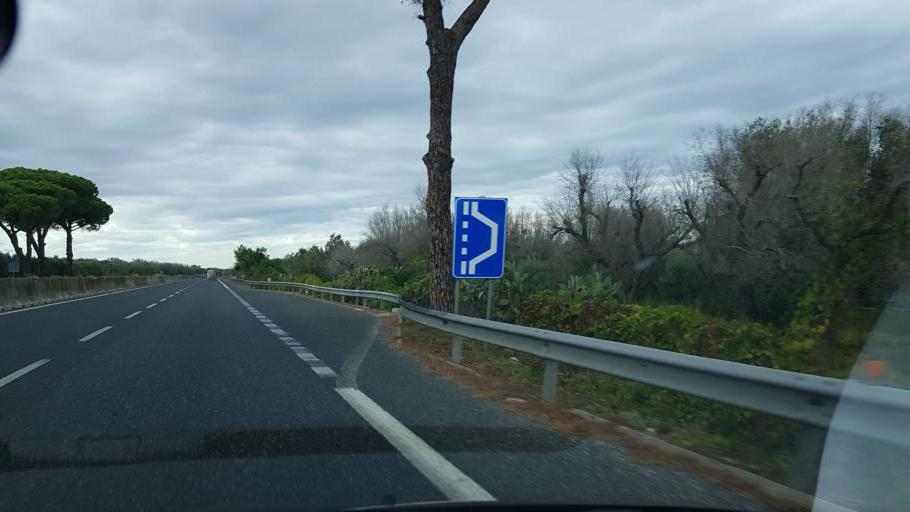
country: IT
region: Apulia
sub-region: Provincia di Brindisi
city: Torchiarolo
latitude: 40.4649
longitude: 18.0560
